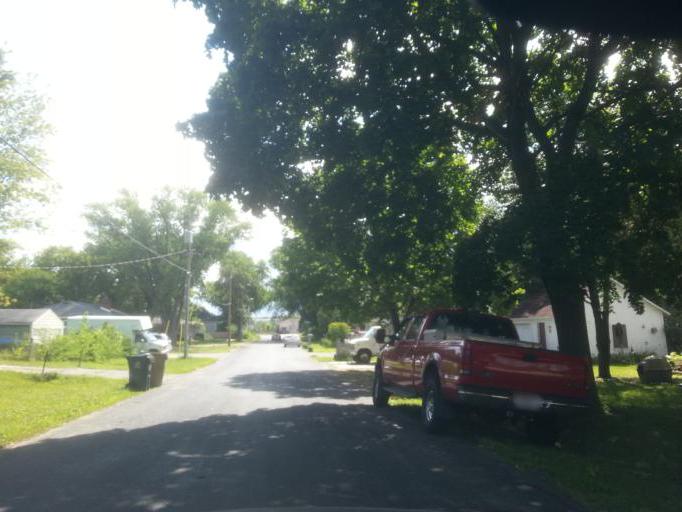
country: US
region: Wisconsin
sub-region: Dane County
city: Monona
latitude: 43.1090
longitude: -89.3281
